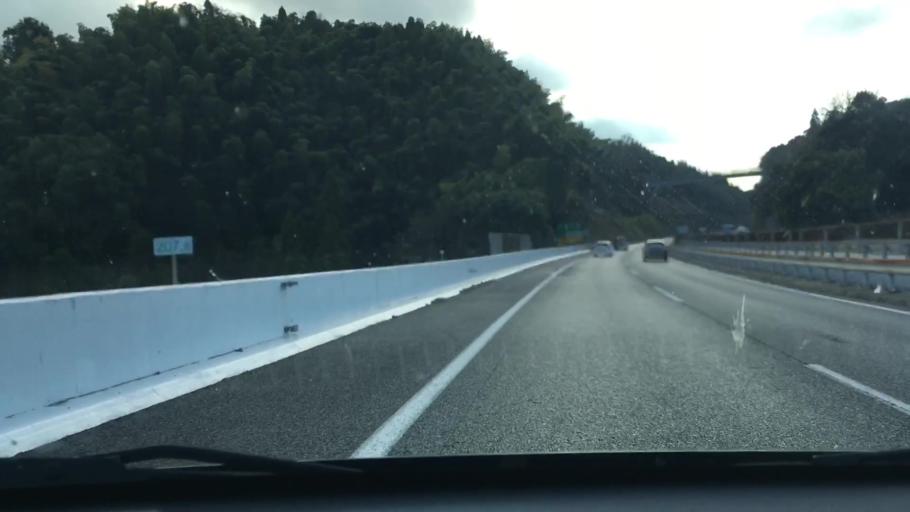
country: JP
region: Kumamoto
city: Yatsushiro
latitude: 32.5500
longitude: 130.6921
